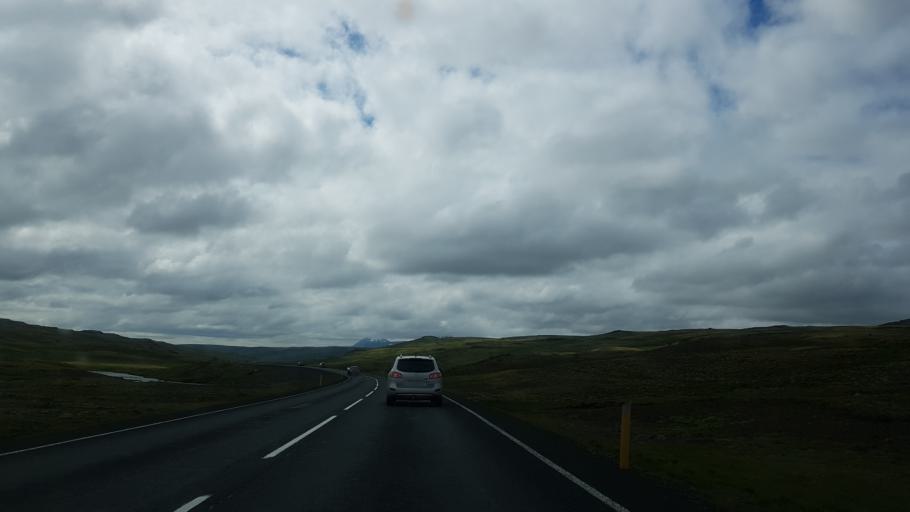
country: IS
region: West
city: Borgarnes
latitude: 64.9284
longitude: -21.0980
